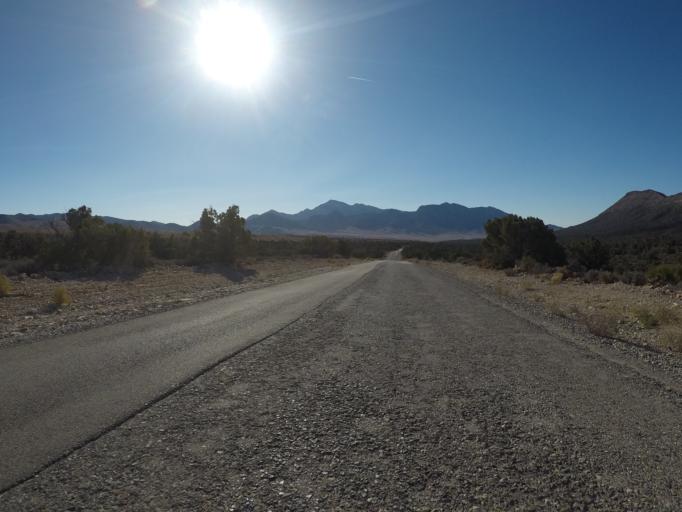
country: US
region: Nevada
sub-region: Clark County
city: Summerlin South
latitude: 36.0678
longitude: -115.5615
